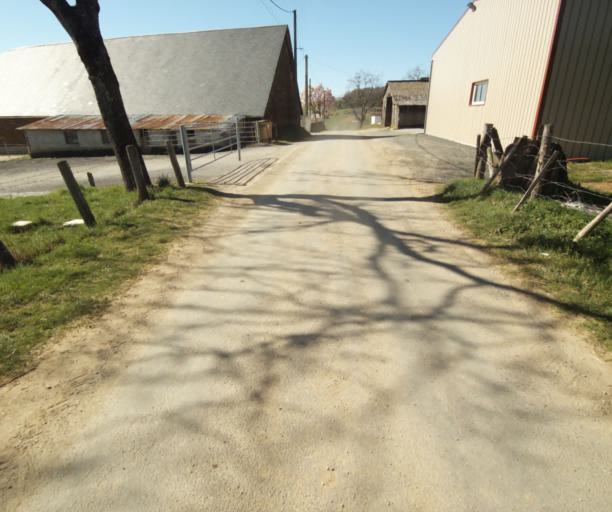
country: FR
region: Limousin
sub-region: Departement de la Correze
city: Seilhac
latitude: 45.3485
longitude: 1.7280
